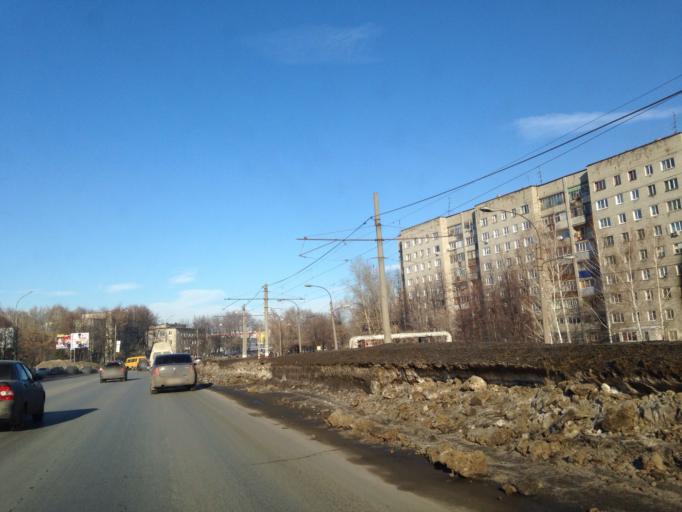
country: RU
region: Ulyanovsk
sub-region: Ulyanovskiy Rayon
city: Ulyanovsk
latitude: 54.3094
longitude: 48.3504
